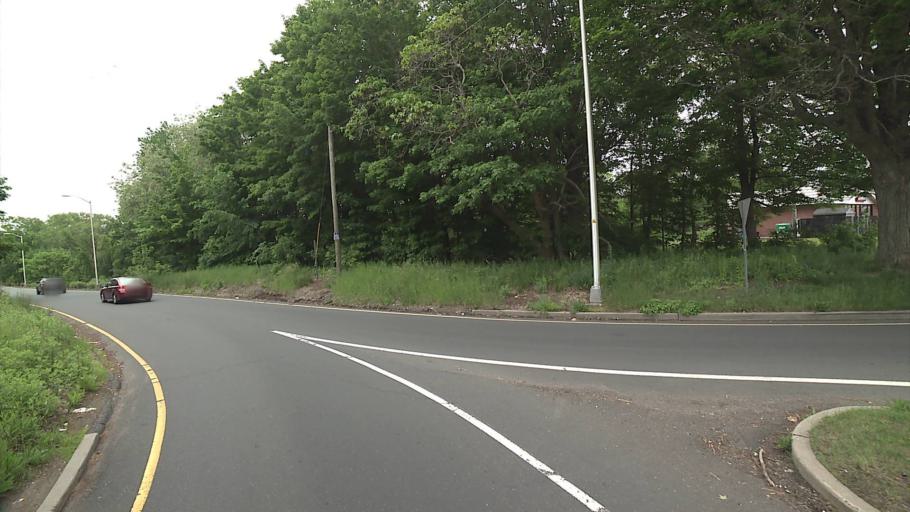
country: US
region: Connecticut
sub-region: New Haven County
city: Meriden
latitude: 41.5269
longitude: -72.7723
